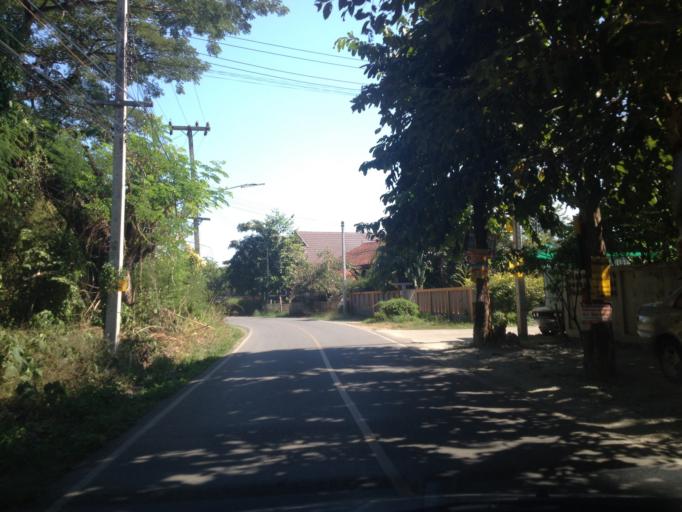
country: TH
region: Chiang Mai
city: Hang Dong
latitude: 18.6853
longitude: 98.9036
